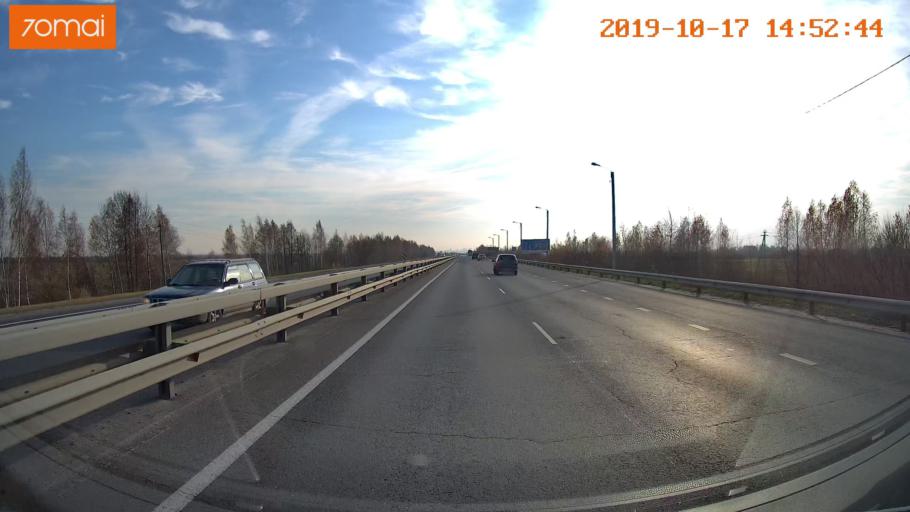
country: RU
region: Rjazan
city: Polyany
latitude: 54.7037
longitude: 39.8436
